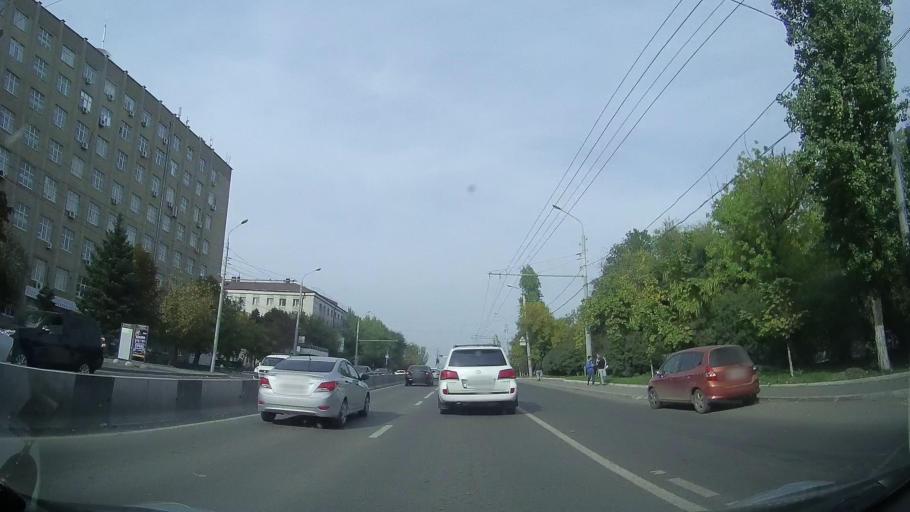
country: RU
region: Rostov
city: Rostov-na-Donu
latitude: 47.2383
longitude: 39.7135
